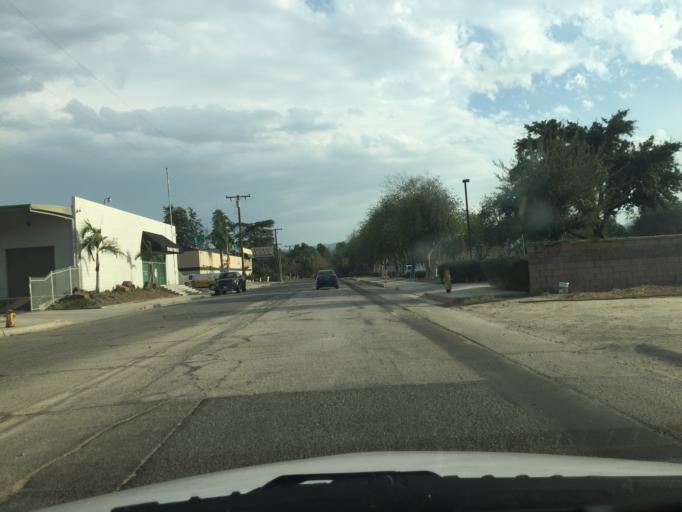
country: US
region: California
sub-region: San Bernardino County
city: Redlands
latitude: 34.0623
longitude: -117.1958
